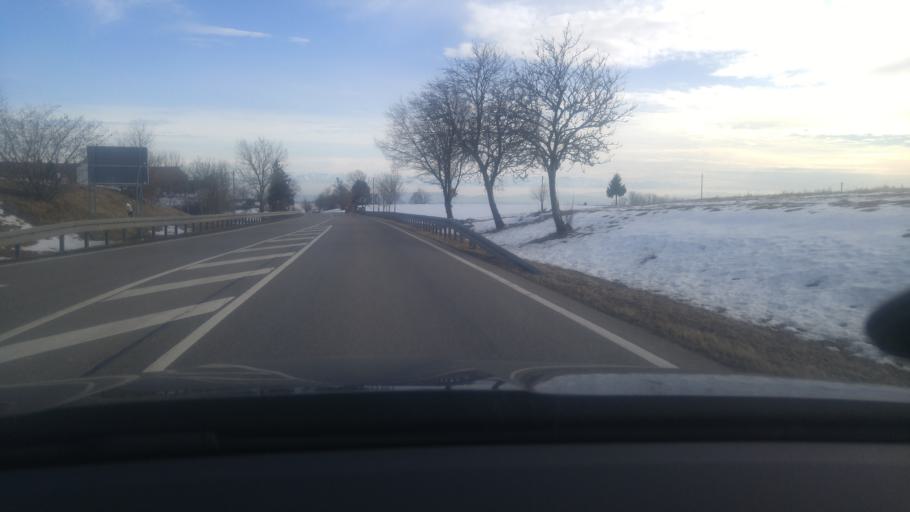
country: DE
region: Baden-Wuerttemberg
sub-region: Freiburg Region
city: Hochenschwand
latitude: 47.7041
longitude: 8.1439
